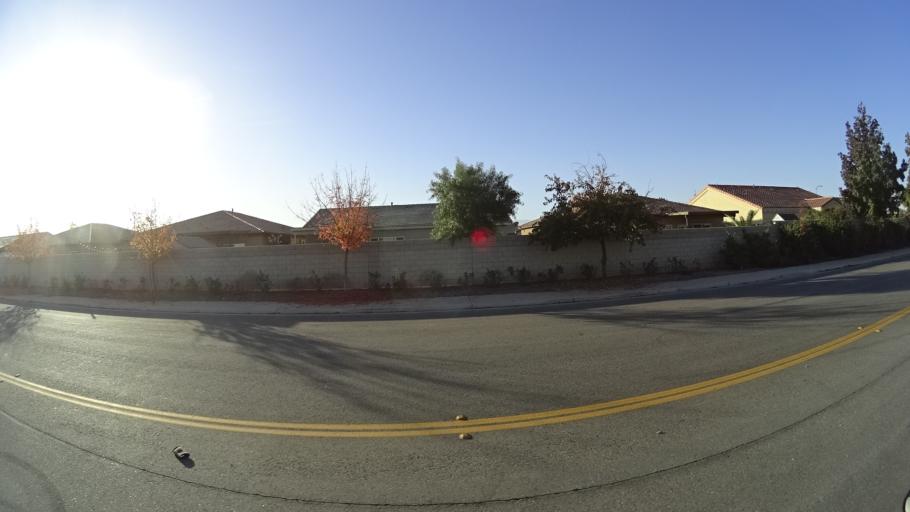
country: US
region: California
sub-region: Kern County
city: Greenfield
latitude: 35.2742
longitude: -119.0292
